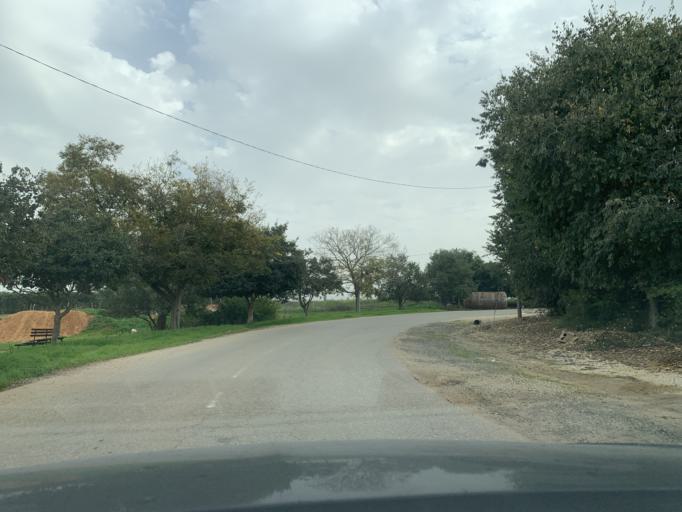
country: IL
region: Central District
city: Tirah
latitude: 32.2180
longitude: 34.9415
